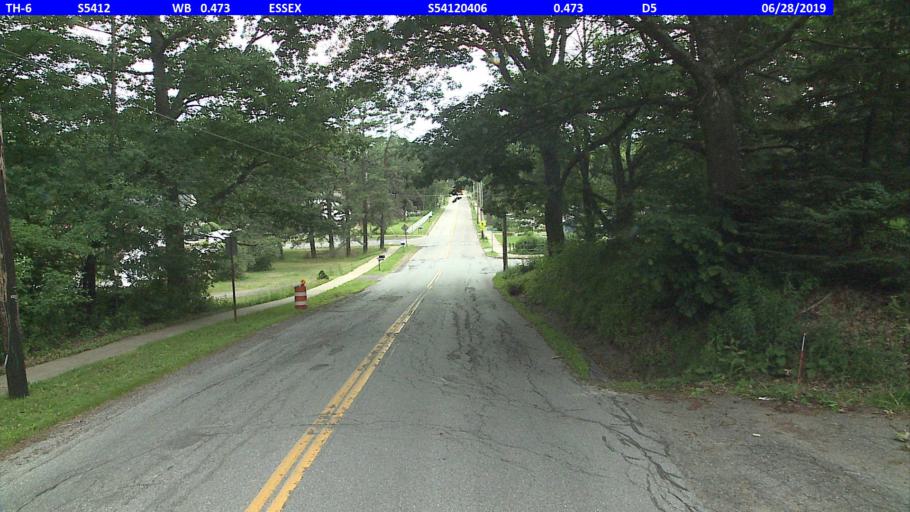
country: US
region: Vermont
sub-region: Chittenden County
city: Essex Junction
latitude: 44.5051
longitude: -73.1271
